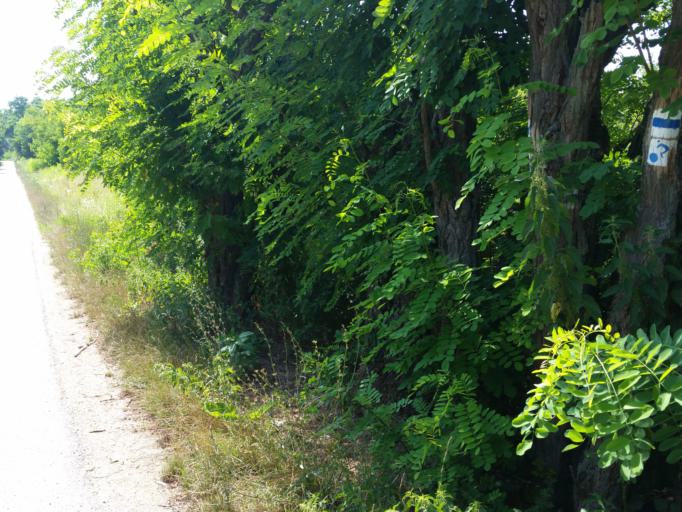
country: HU
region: Vas
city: Sarvar
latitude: 47.2085
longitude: 17.0056
